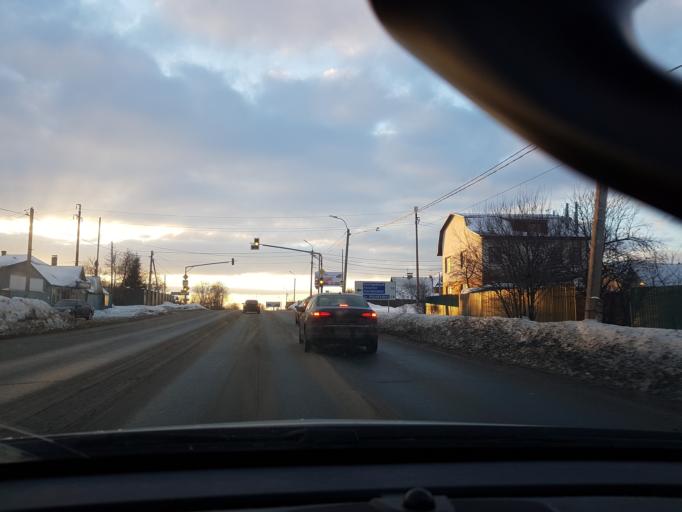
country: RU
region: Moskovskaya
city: Istra
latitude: 55.9065
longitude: 36.9350
